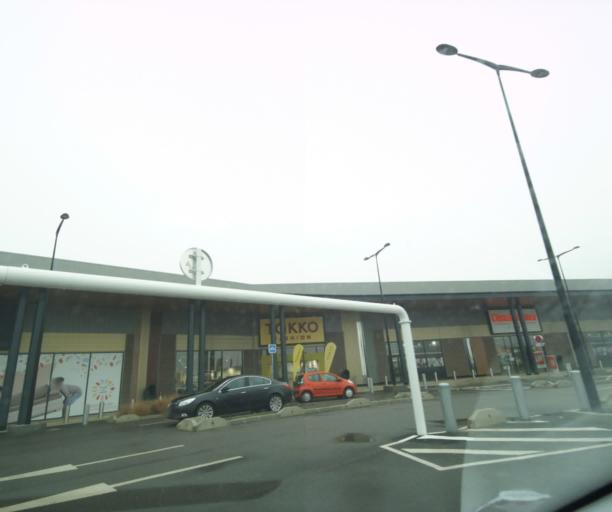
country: FR
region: Ile-de-France
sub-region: Departement de Seine-et-Marne
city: Saint-Mard
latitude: 49.0344
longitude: 2.6817
